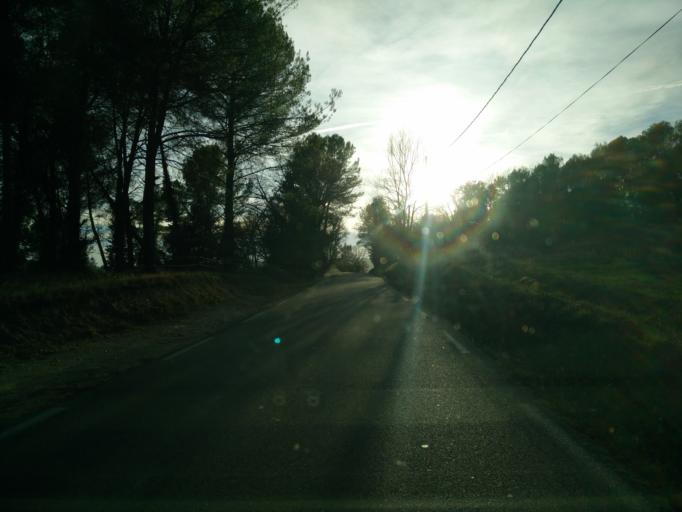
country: FR
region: Provence-Alpes-Cote d'Azur
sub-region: Departement du Var
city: Callian
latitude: 43.6128
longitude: 6.7388
